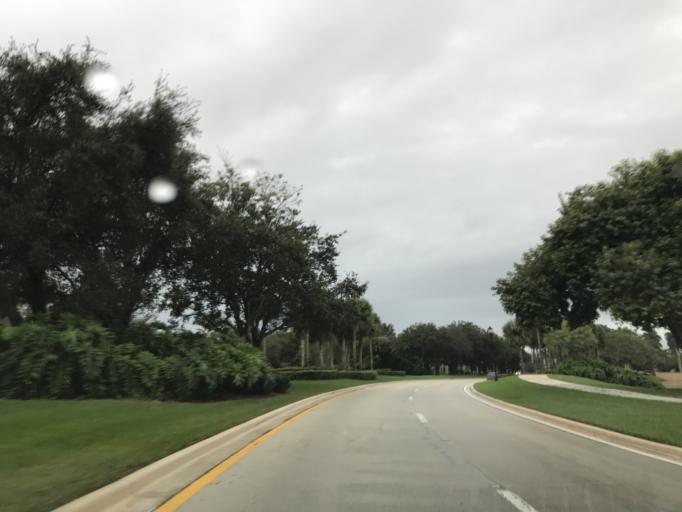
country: US
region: Florida
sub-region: Broward County
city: Coral Springs
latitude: 26.3075
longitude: -80.2819
